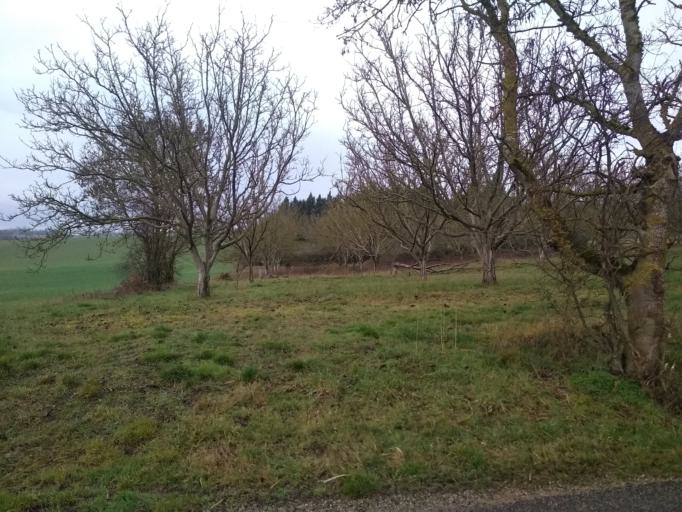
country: FR
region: Midi-Pyrenees
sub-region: Departement du Gers
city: Pujaudran
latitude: 43.6695
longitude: 1.0305
